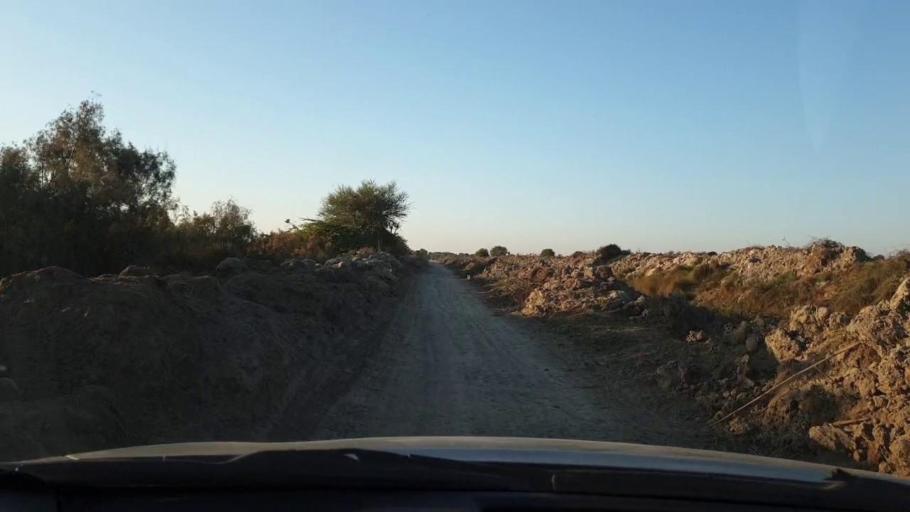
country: PK
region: Sindh
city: Jhol
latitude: 25.8897
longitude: 68.8943
